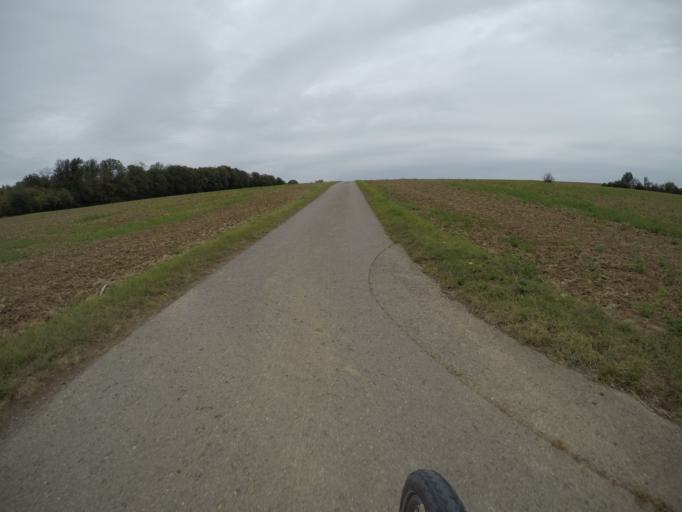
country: DE
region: Baden-Wuerttemberg
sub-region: Regierungsbezirk Stuttgart
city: Eberdingen
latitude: 48.8769
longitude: 8.9875
